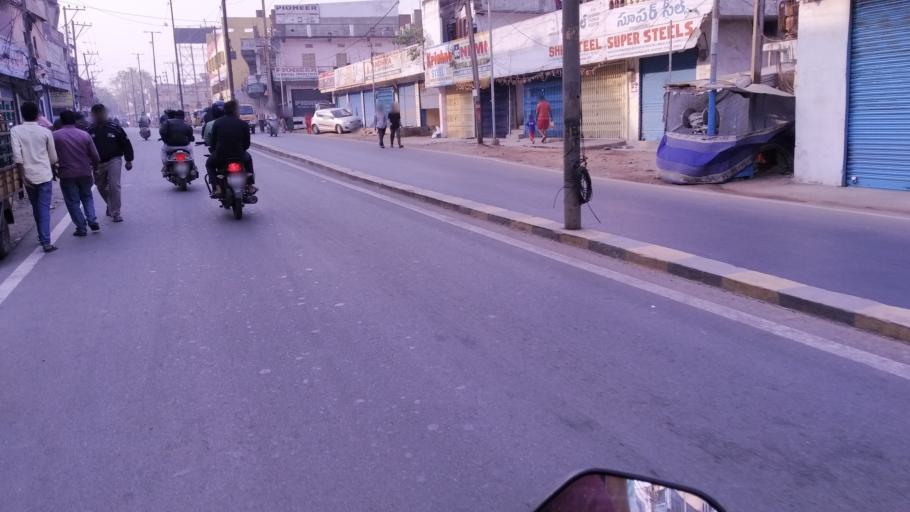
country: IN
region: Telangana
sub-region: Rangareddi
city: Quthbullapur
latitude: 17.4617
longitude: 78.4494
